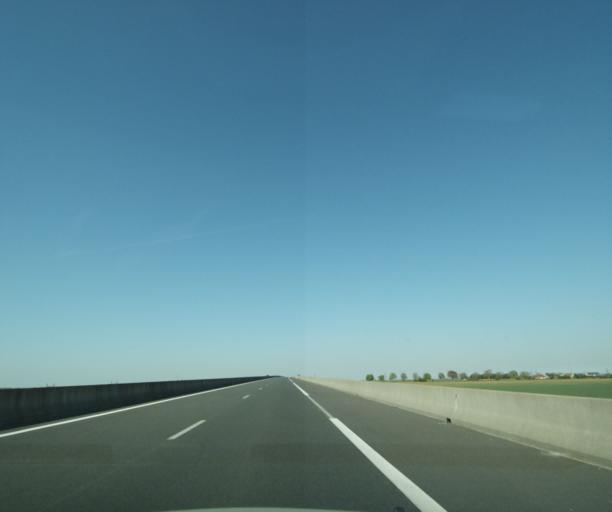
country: FR
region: Centre
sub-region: Departement du Loiret
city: Chevilly
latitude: 48.0457
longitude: 1.8837
